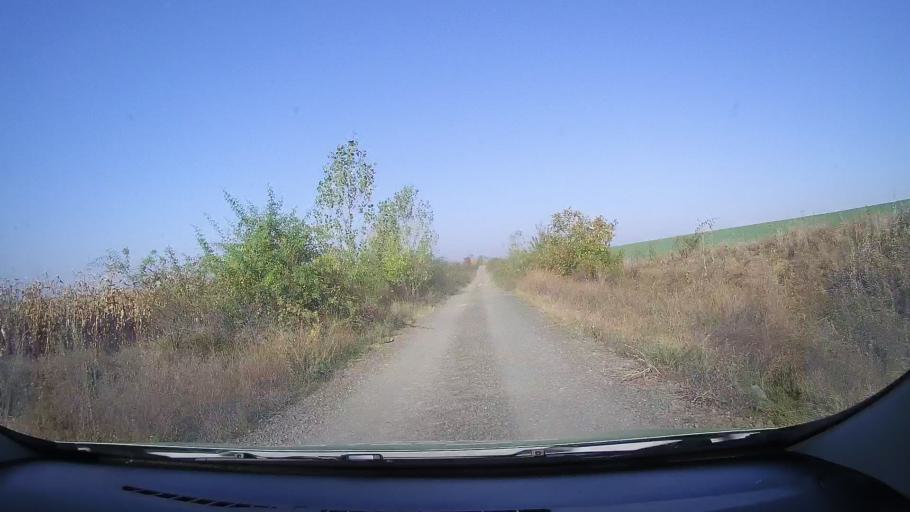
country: RO
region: Satu Mare
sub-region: Comuna Sauca
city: Sauca
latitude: 47.4825
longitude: 22.4660
